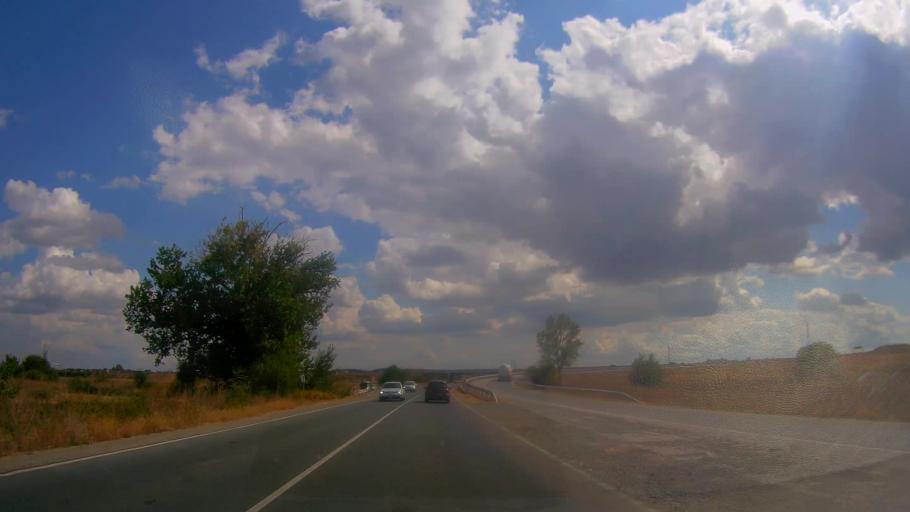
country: BG
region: Yambol
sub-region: Obshtina Yambol
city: Yambol
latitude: 42.5404
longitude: 26.4162
